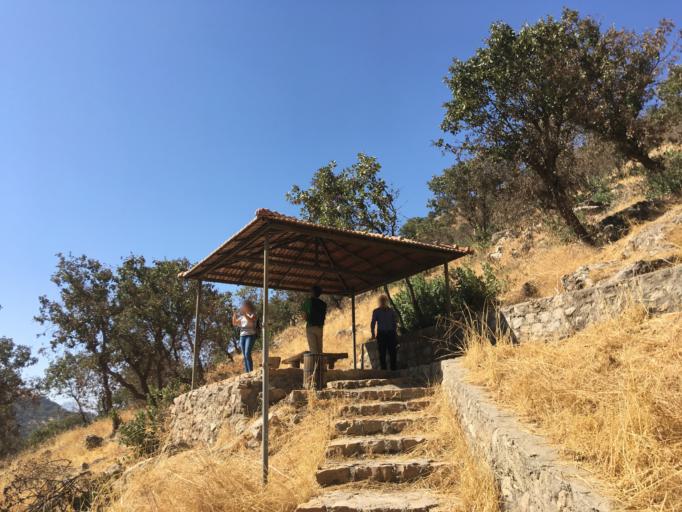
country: IQ
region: Arbil
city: Mergasur
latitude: 36.8342
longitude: 44.2191
